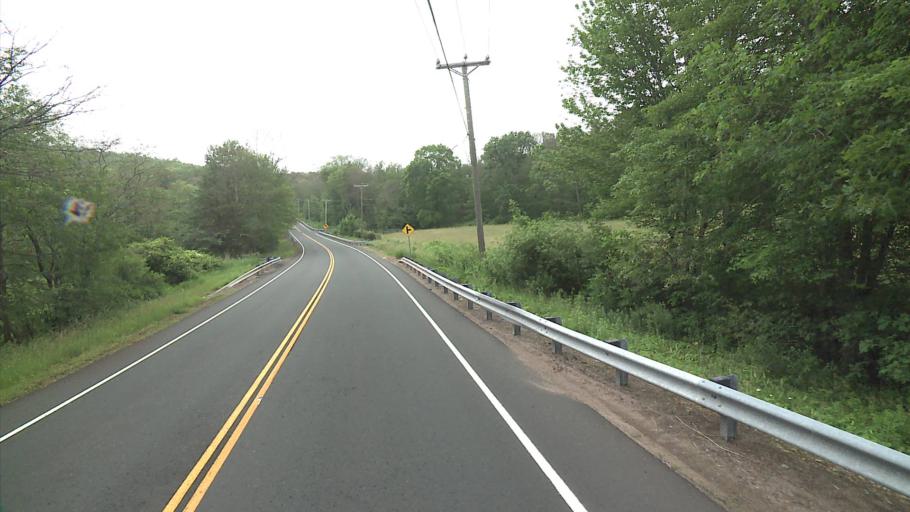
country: US
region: Connecticut
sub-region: Hartford County
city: Terramuggus
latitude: 41.6950
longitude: -72.4545
